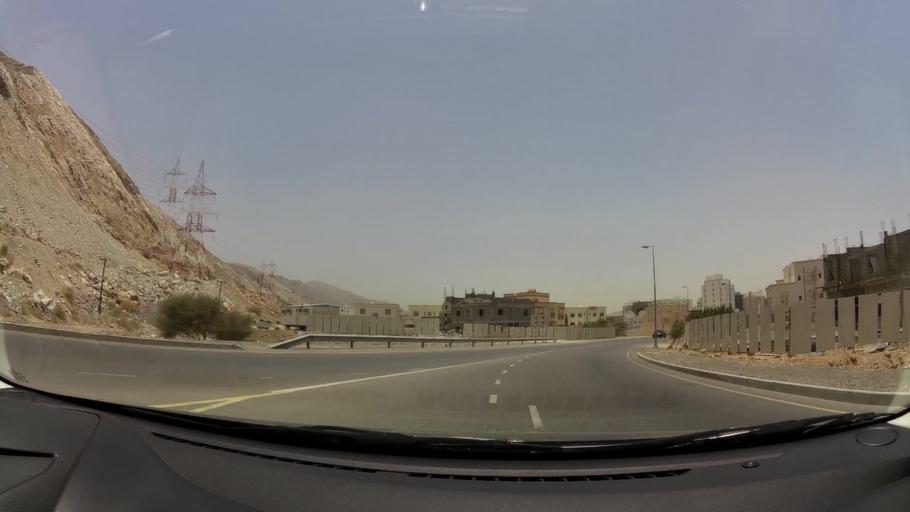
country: OM
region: Muhafazat Masqat
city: Bawshar
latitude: 23.5639
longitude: 58.4253
